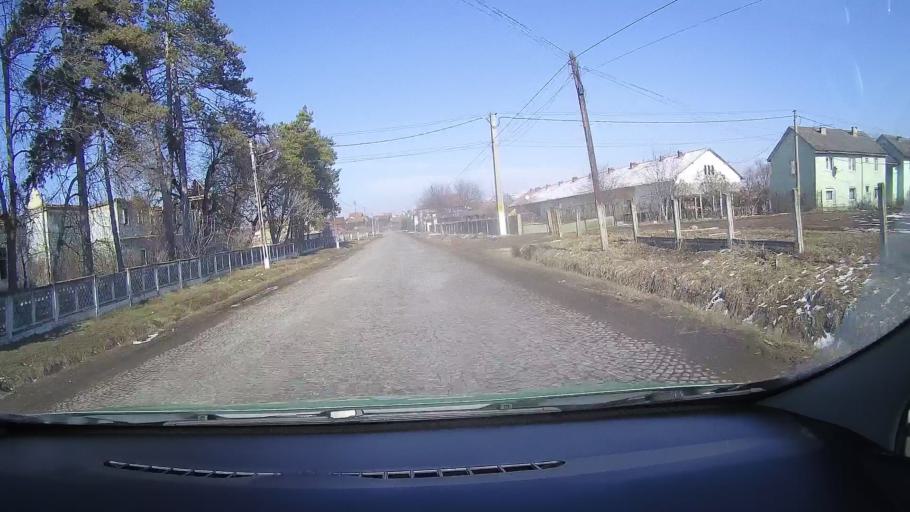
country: RO
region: Brasov
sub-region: Comuna Homorod
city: Homorod
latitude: 46.0370
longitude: 25.2741
